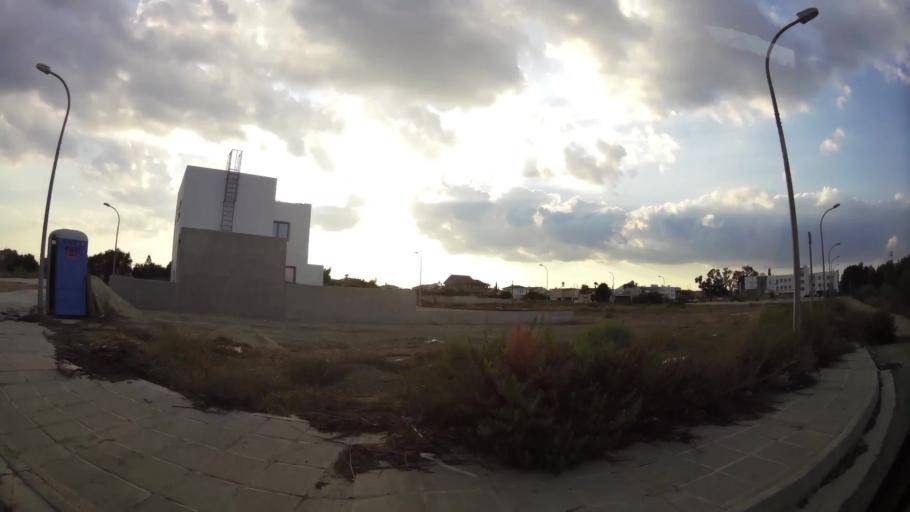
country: CY
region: Larnaka
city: Kiti
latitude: 34.8530
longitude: 33.5850
